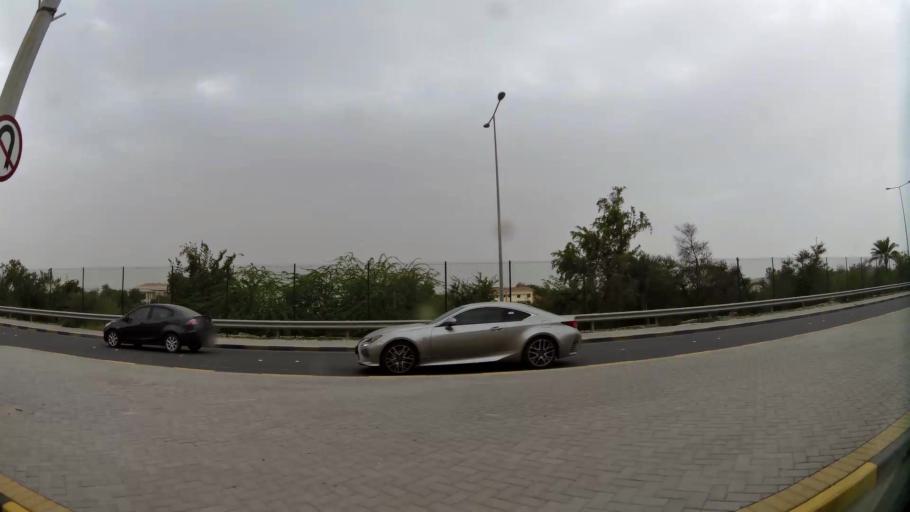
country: BH
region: Northern
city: Ar Rifa'
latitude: 26.1389
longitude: 50.5431
